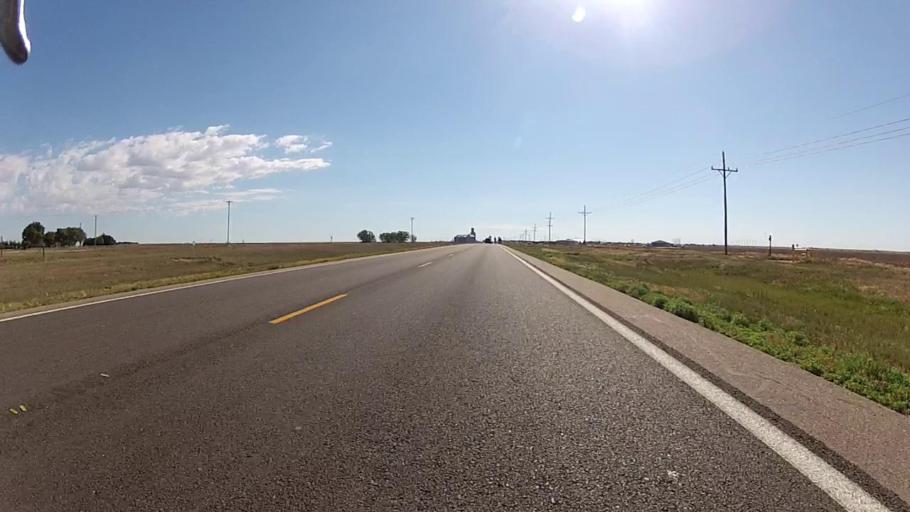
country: US
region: Kansas
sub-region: Gray County
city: Cimarron
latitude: 37.5903
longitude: -100.4743
